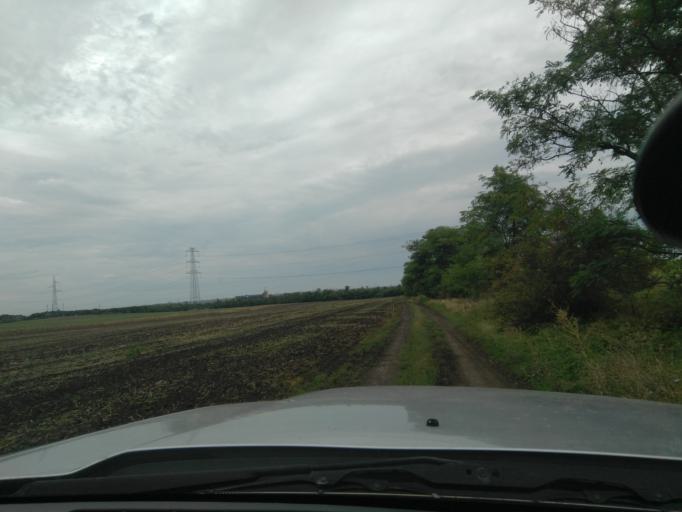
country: HU
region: Fejer
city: Martonvasar
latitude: 47.3543
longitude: 18.7929
